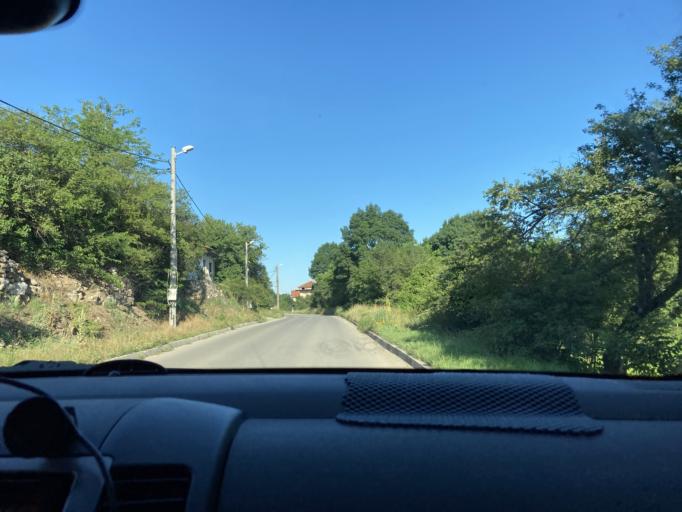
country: BG
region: Sofiya
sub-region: Obshtina Slivnitsa
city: Slivnitsa
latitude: 42.8459
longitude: 22.9956
